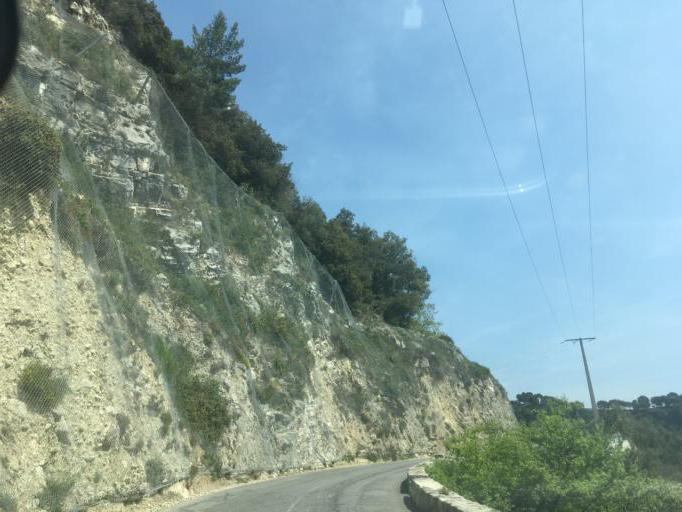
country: FR
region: Provence-Alpes-Cote d'Azur
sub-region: Departement des Alpes-Maritimes
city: Saint-Martin-du-Var
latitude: 43.8270
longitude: 7.1971
